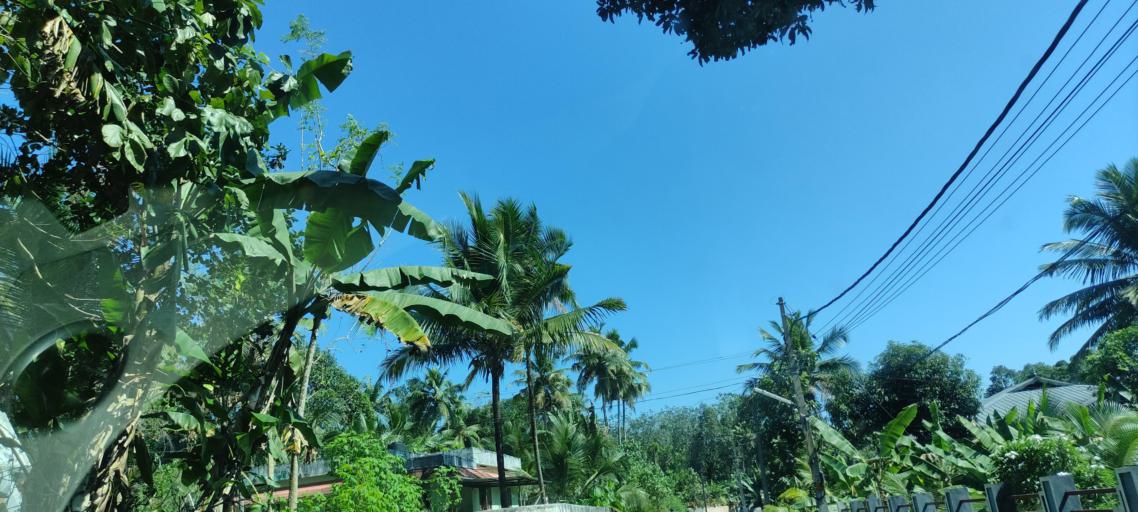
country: IN
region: Kerala
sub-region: Pattanamtitta
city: Adur
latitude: 9.0951
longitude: 76.7350
